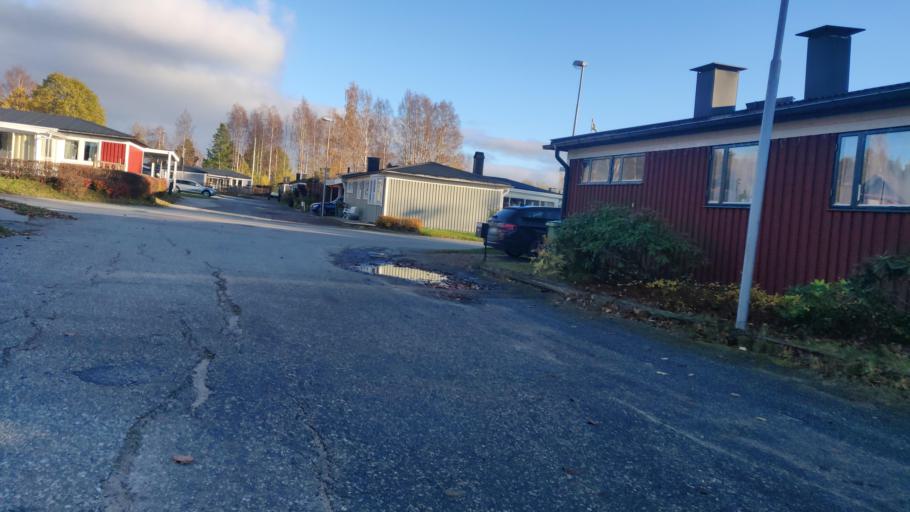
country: SE
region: Vaesternorrland
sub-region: Sundsvalls Kommun
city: Nolby
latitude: 62.2738
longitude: 17.3688
